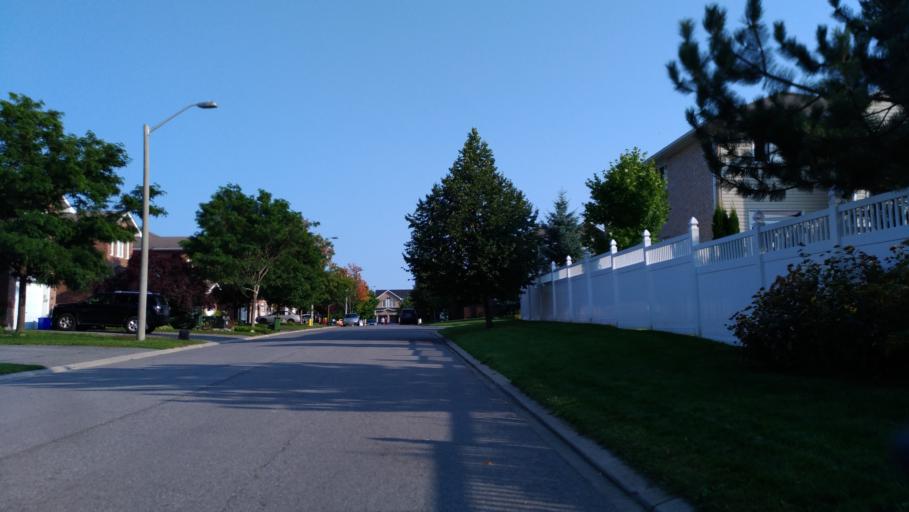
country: CA
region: Ontario
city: Bells Corners
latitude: 45.3547
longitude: -75.9379
